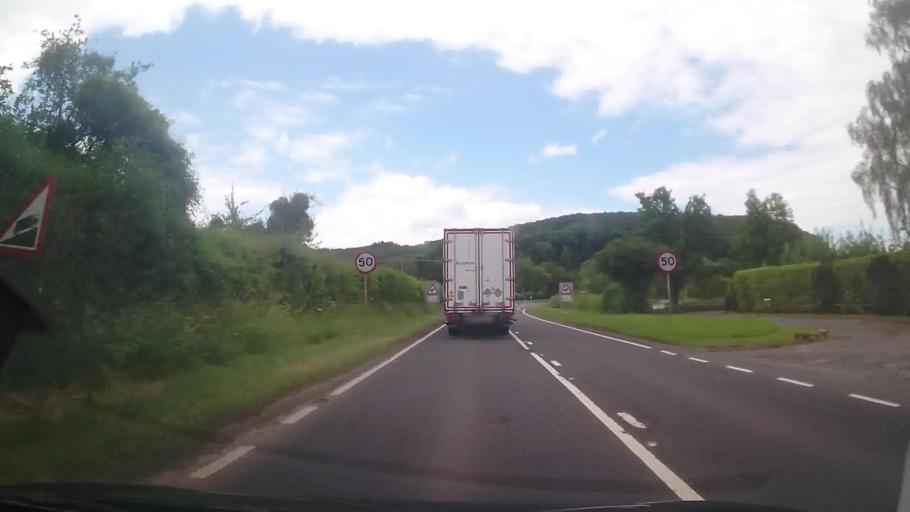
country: GB
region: England
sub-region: Herefordshire
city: Dinmore
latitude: 52.1474
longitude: -2.7273
